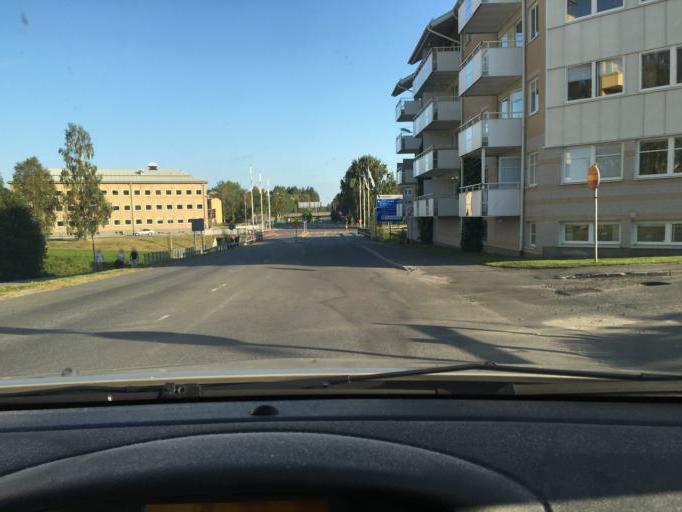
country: SE
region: Norrbotten
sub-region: Bodens Kommun
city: Boden
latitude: 65.8239
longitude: 21.6894
